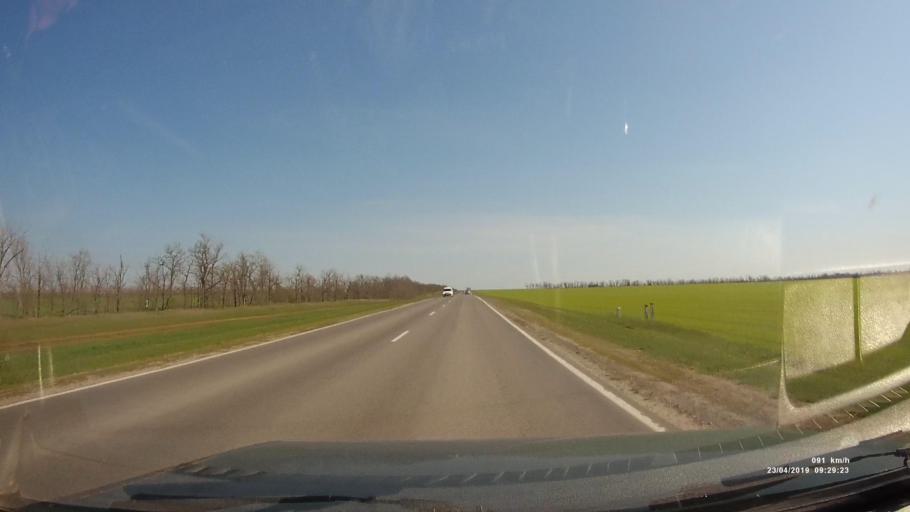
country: RU
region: Rostov
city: Gundorovskiy
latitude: 46.7605
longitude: 41.8049
